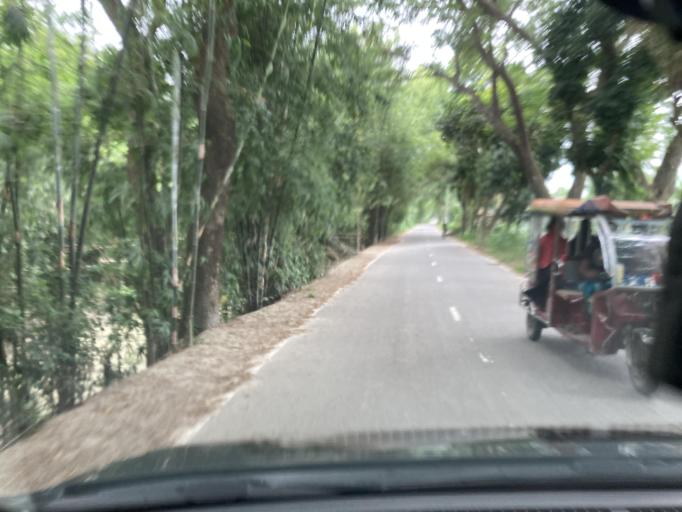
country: BD
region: Dhaka
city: Dohar
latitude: 23.7771
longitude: 90.0666
